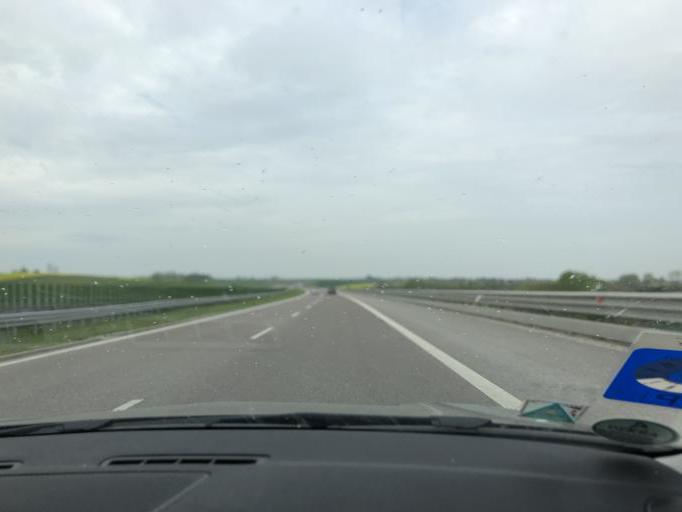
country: PL
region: Subcarpathian Voivodeship
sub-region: Powiat jaroslawski
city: Wierzbna
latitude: 50.0146
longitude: 22.5921
